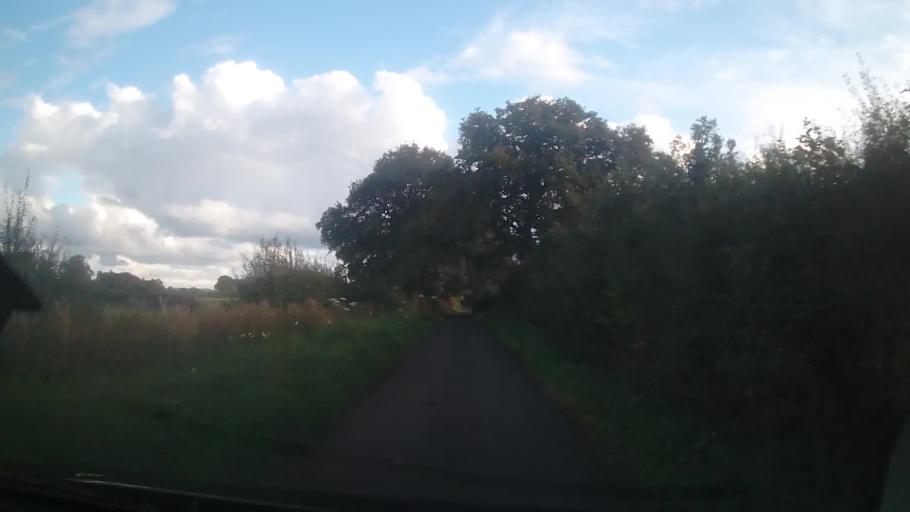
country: GB
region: England
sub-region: Shropshire
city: Wem
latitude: 52.8801
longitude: -2.7304
